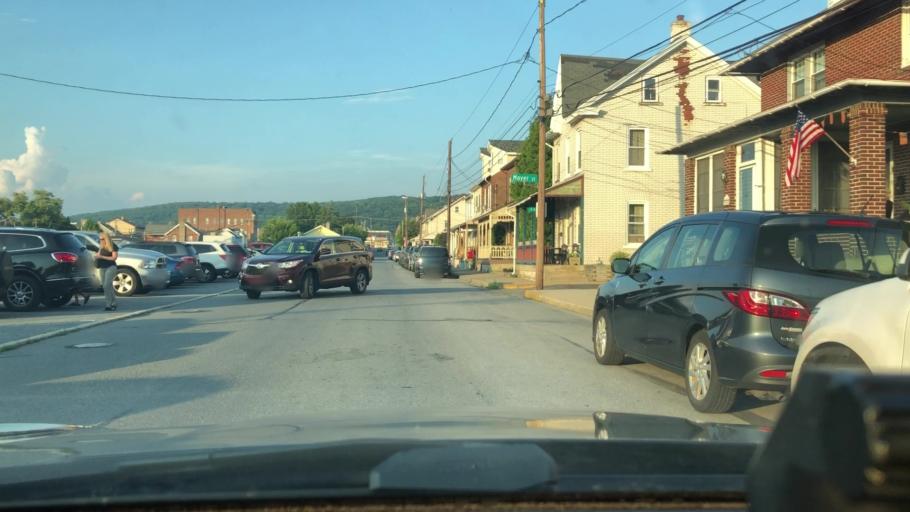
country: US
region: Pennsylvania
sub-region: Lehigh County
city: Emmaus
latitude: 40.5325
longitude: -75.4950
